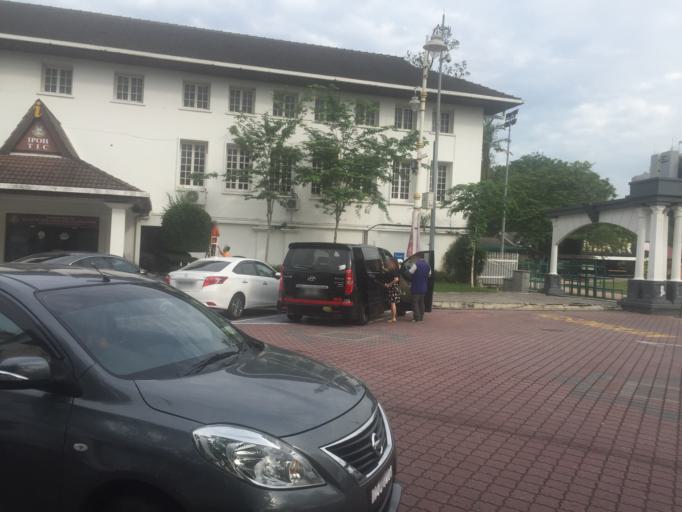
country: MY
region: Perak
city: Ipoh
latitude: 4.5980
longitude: 101.0763
